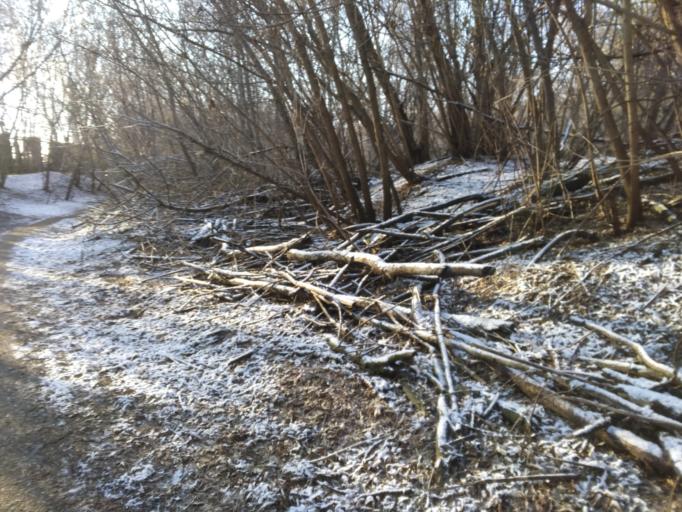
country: RU
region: Kirov
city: Vyatskiye Polyany
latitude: 56.2385
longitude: 51.0679
